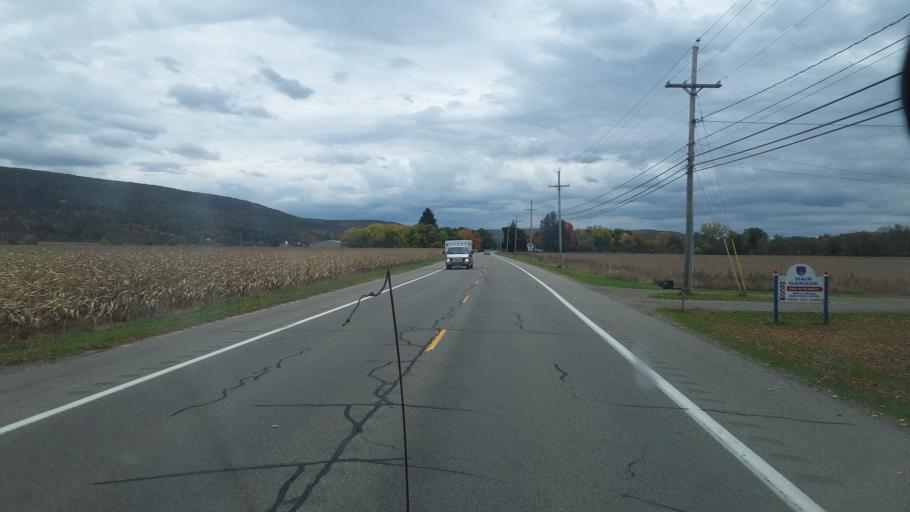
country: US
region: New York
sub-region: Allegany County
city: Belmont
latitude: 42.2061
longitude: -78.0105
